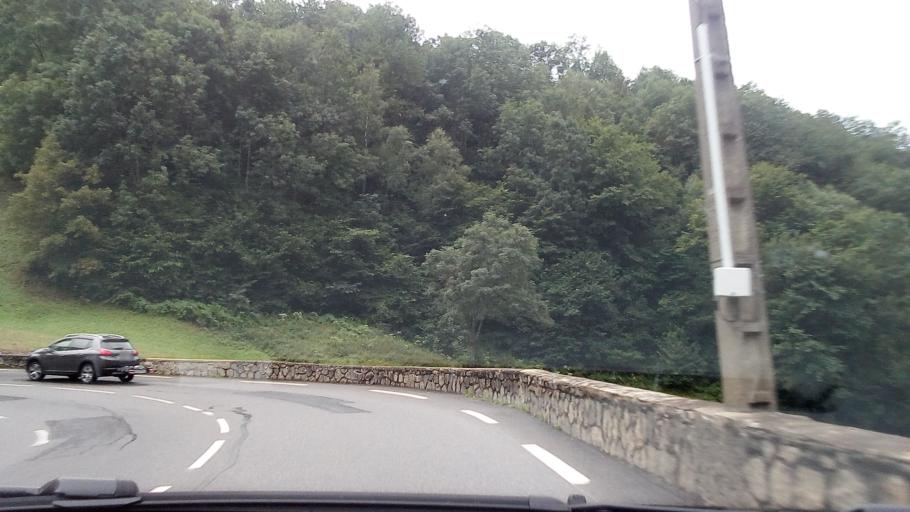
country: FR
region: Midi-Pyrenees
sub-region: Departement des Hautes-Pyrenees
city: Luz-Saint-Sauveur
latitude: 42.8829
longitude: 0.0395
